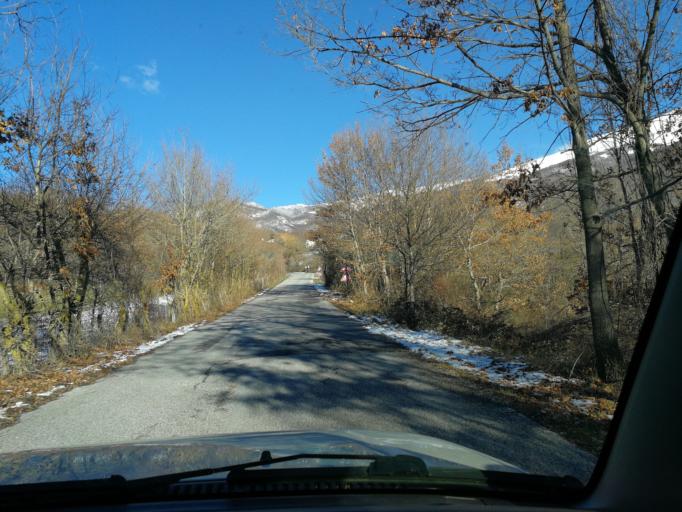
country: IT
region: Latium
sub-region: Provincia di Rieti
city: Amatrice
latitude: 42.6673
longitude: 13.2810
